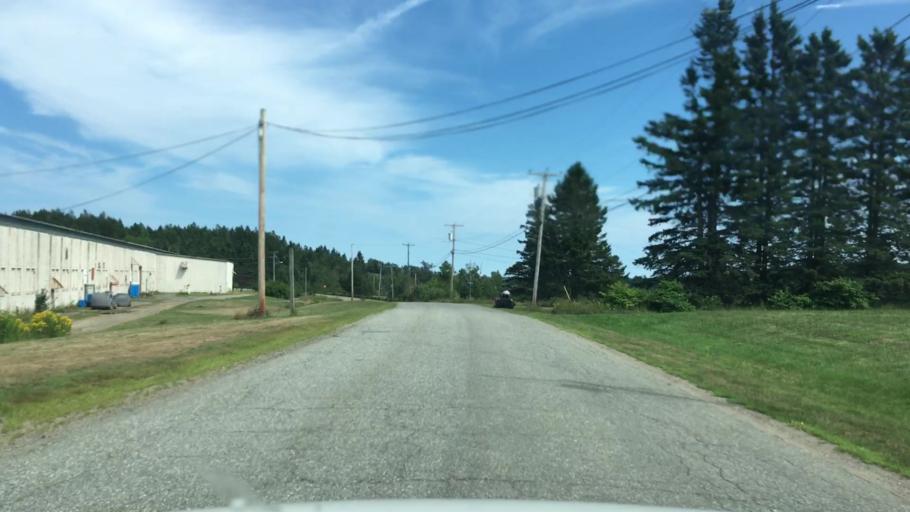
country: US
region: Maine
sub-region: Washington County
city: Eastport
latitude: 44.9269
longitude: -67.0276
